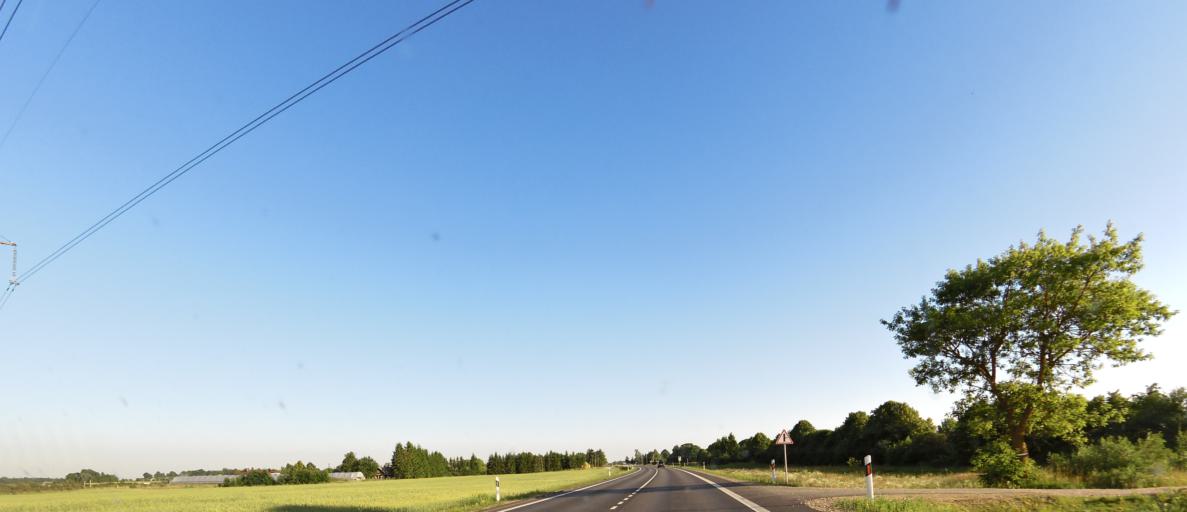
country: LT
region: Panevezys
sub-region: Panevezys City
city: Panevezys
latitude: 55.6356
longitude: 24.3479
